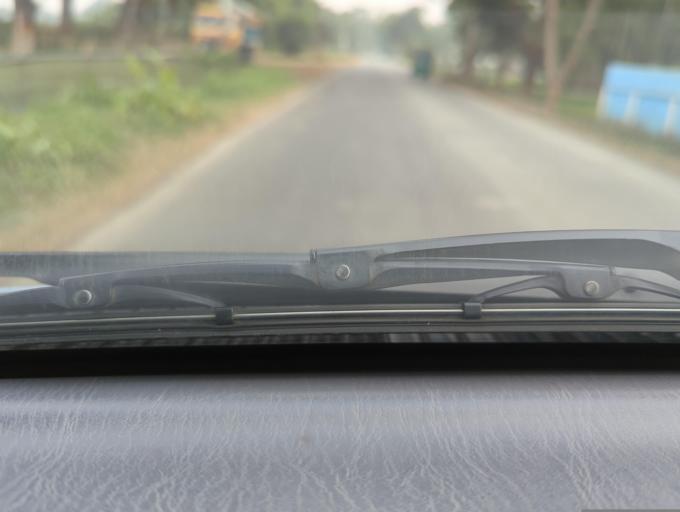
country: BD
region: Sylhet
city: Maulavi Bazar
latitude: 24.5061
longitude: 91.7335
